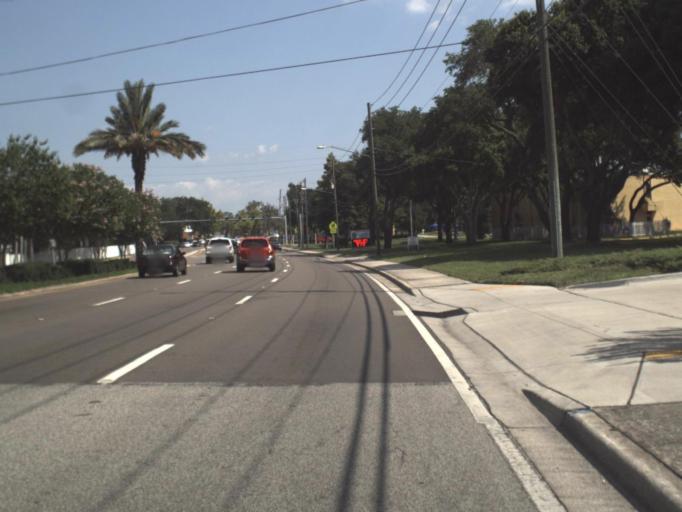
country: US
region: Florida
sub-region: Pinellas County
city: Largo
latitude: 27.9072
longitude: -82.7871
